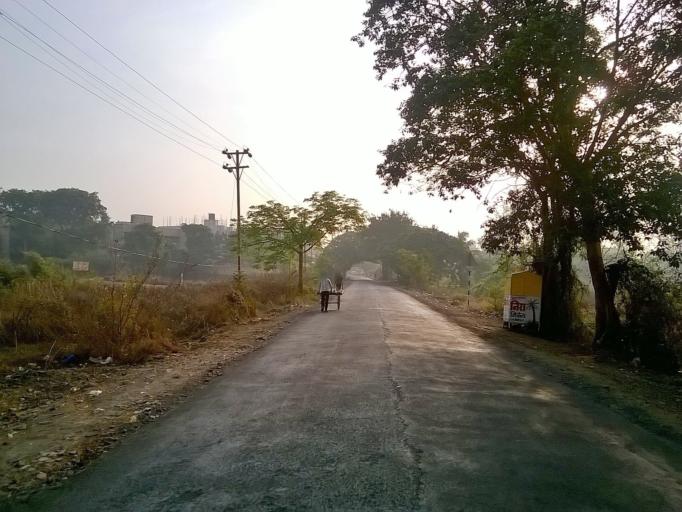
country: IN
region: Maharashtra
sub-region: Raigarh
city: Kalundri
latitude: 19.0039
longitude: 73.1497
